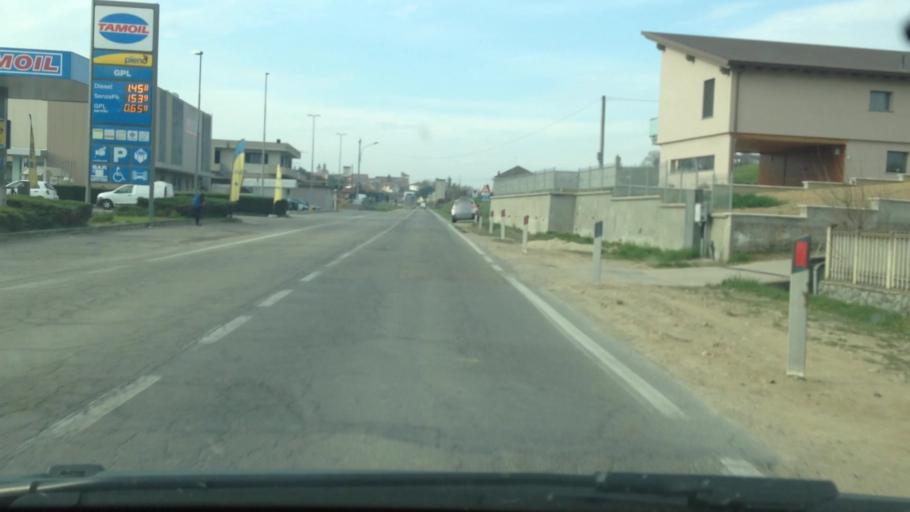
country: IT
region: Piedmont
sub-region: Provincia di Asti
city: San Damiano d'Asti
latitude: 44.8449
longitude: 8.0705
